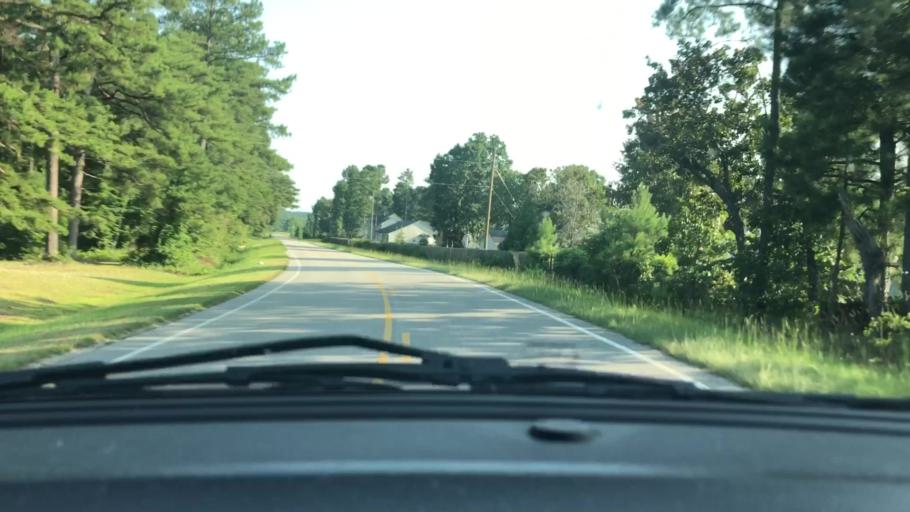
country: US
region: North Carolina
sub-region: Lee County
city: Broadway
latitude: 35.3438
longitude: -79.0724
